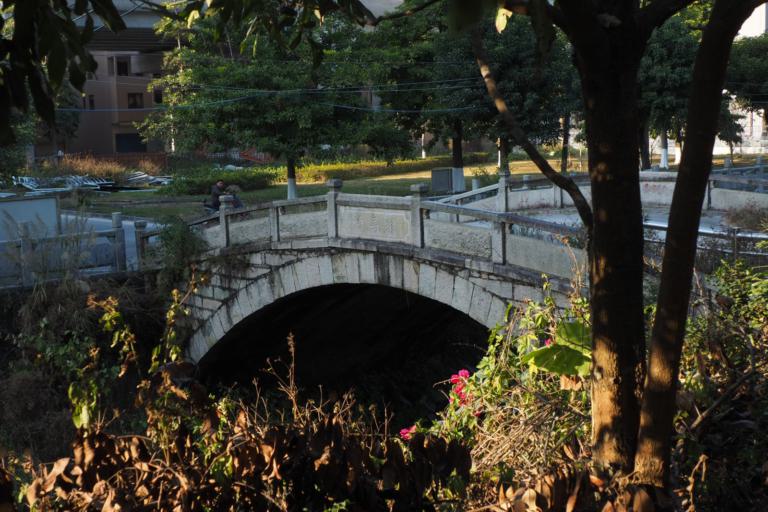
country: CN
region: Guangdong
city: Huancheng
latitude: 22.4429
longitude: 113.3948
